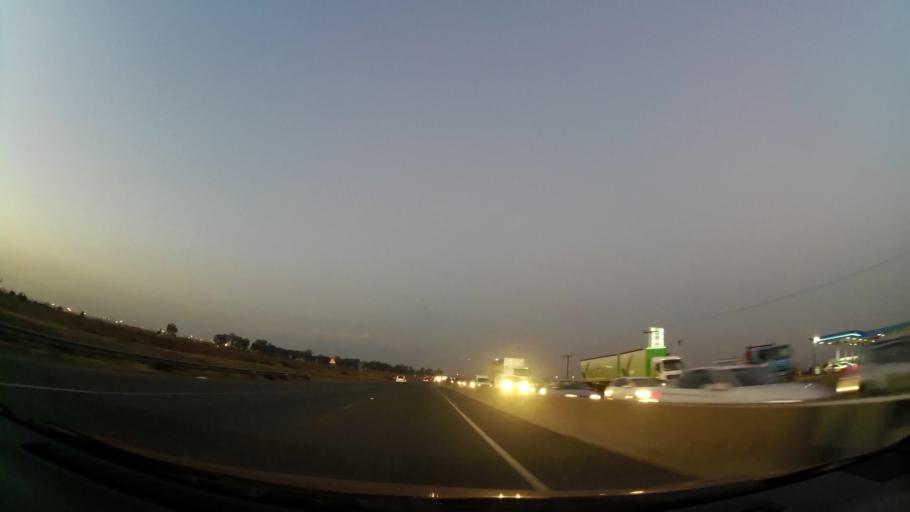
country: ZA
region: Gauteng
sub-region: City of Johannesburg Metropolitan Municipality
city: Soweto
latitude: -26.2969
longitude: 27.8243
